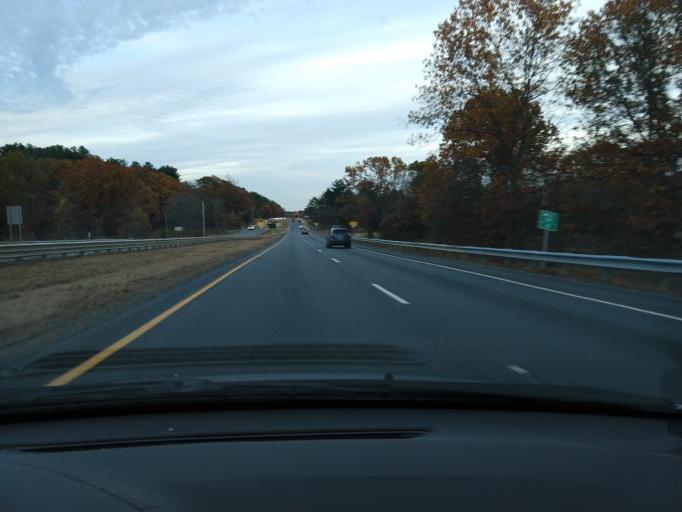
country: US
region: Massachusetts
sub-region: Middlesex County
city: West Concord
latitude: 42.4696
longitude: -71.4092
